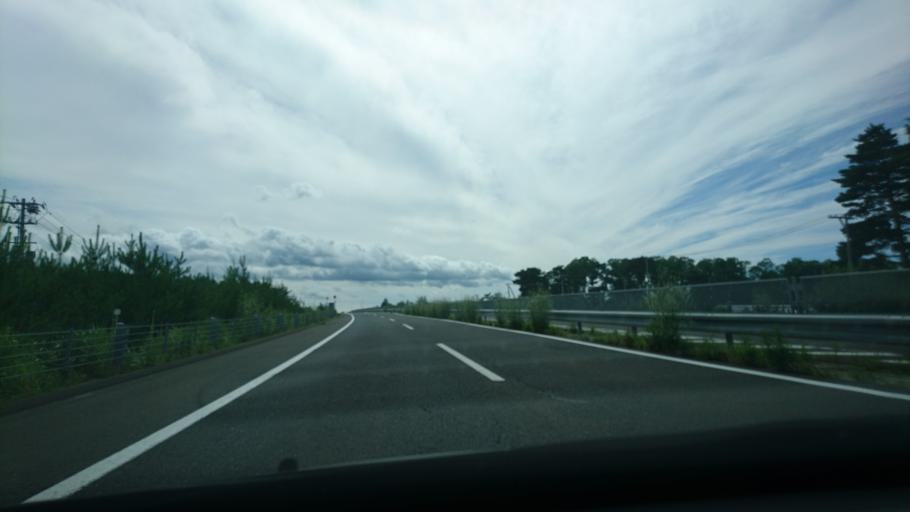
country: JP
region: Aomori
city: Hachinohe
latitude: 40.4838
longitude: 141.5636
